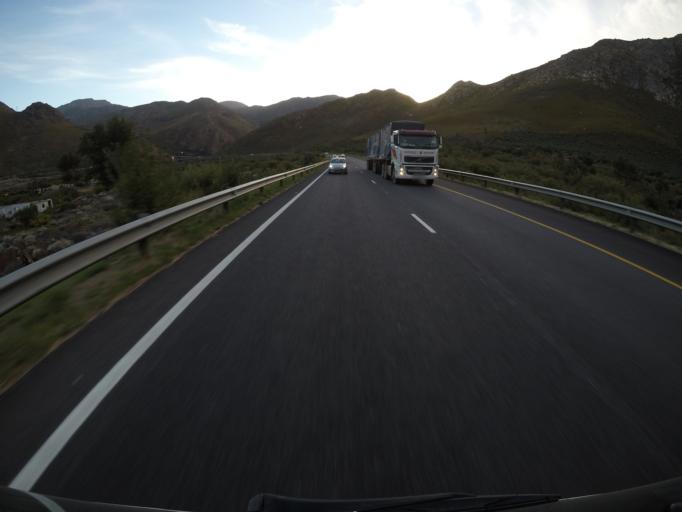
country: ZA
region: Western Cape
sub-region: Cape Winelands District Municipality
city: Paarl
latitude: -33.7267
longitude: 19.1244
